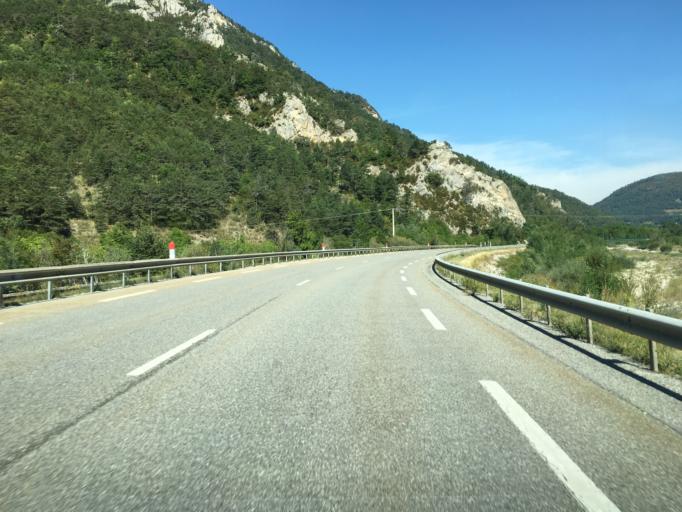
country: FR
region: Provence-Alpes-Cote d'Azur
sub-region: Departement des Hautes-Alpes
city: Veynes
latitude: 44.5961
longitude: 5.7100
